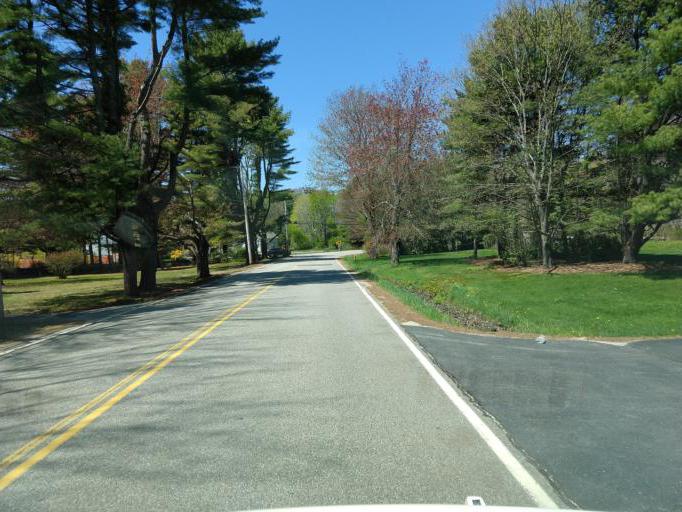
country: US
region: Maine
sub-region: York County
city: Old Orchard Beach
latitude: 43.4696
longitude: -70.3931
